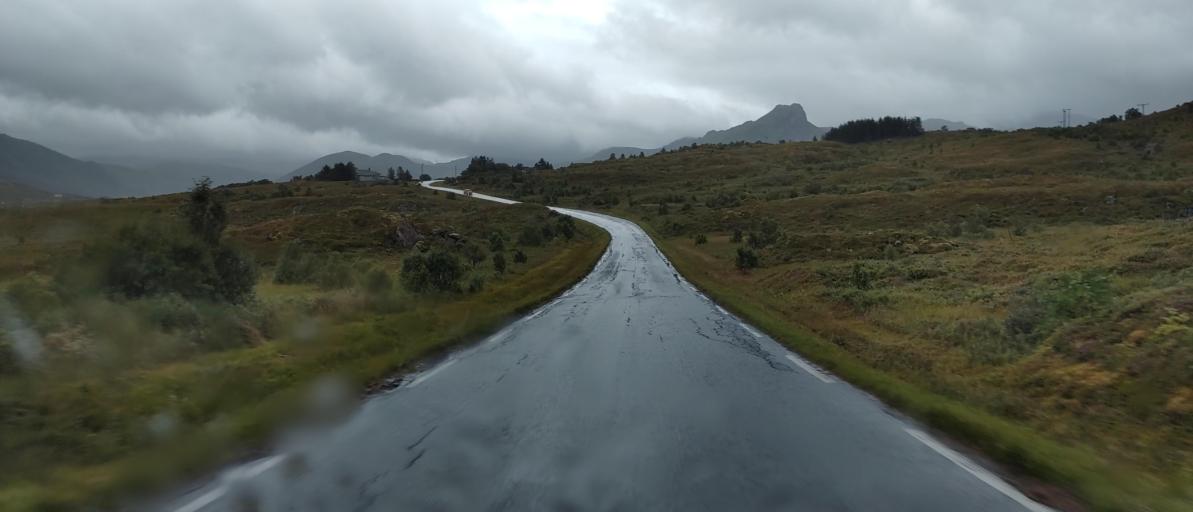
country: NO
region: Nordland
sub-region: Vestvagoy
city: Evjen
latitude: 68.2650
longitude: 13.7701
